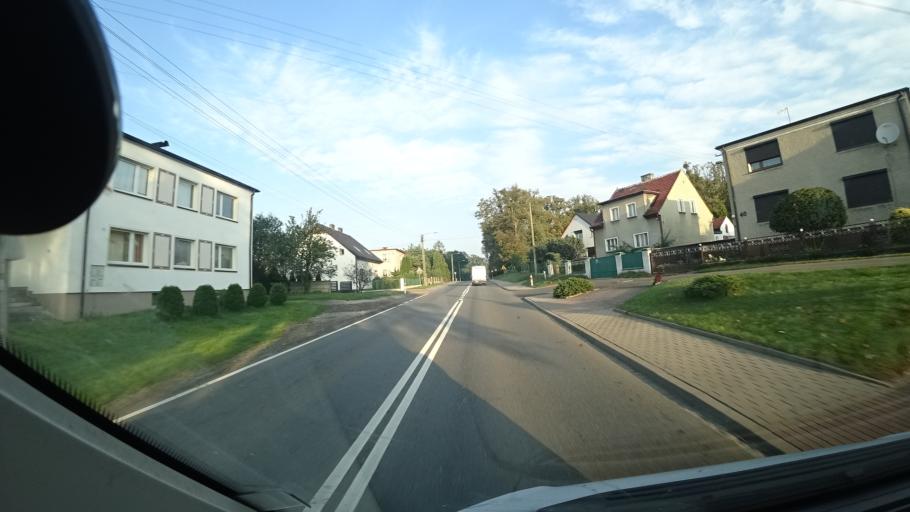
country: PL
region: Opole Voivodeship
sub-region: Powiat strzelecki
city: Ujazd
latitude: 50.3875
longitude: 18.3605
